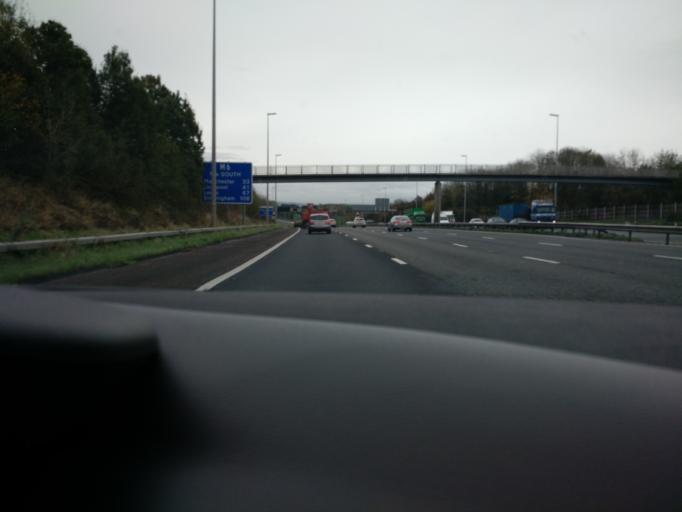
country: GB
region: England
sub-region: Lancashire
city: Goosnargh
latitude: 53.7959
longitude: -2.6787
